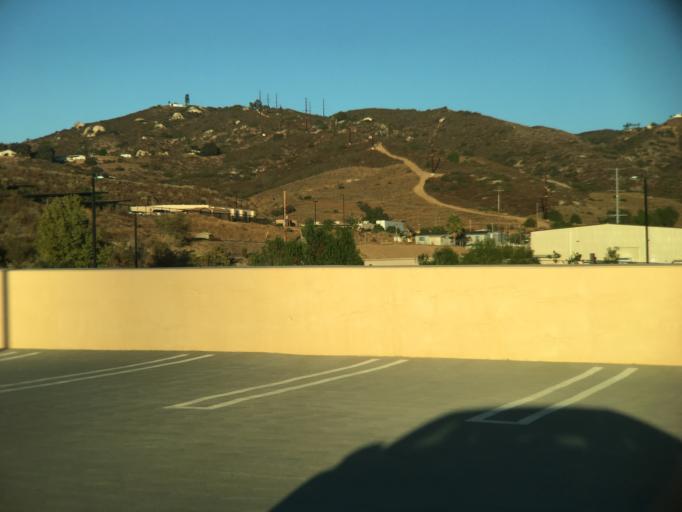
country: US
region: California
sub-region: San Diego County
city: Harbison Canyon
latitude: 32.7872
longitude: -116.8287
